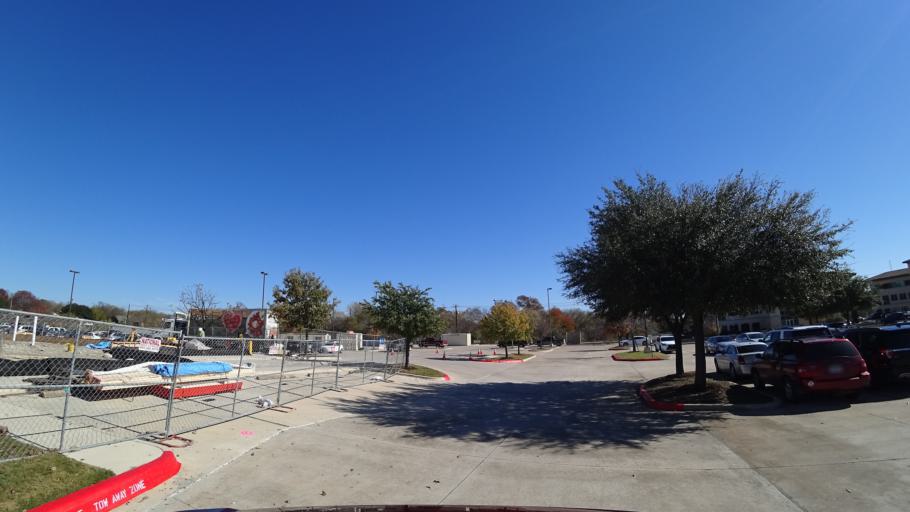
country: US
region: Texas
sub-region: Travis County
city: Wells Branch
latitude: 30.4108
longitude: -97.7037
